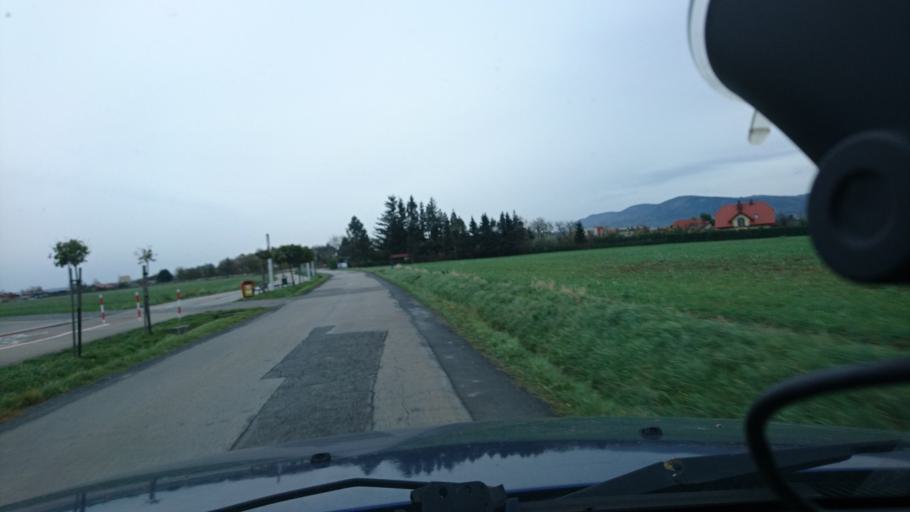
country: PL
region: Silesian Voivodeship
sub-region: Bielsko-Biala
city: Bielsko-Biala
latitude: 49.8048
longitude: 19.0087
